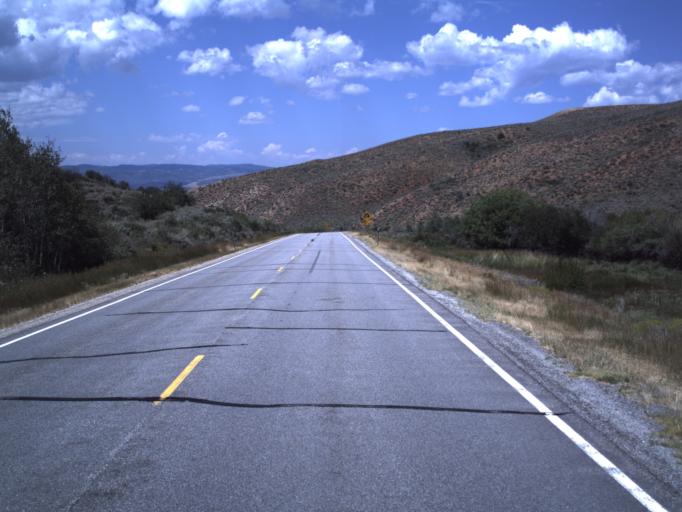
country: US
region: Utah
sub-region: Rich County
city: Randolph
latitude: 41.8129
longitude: -111.2659
